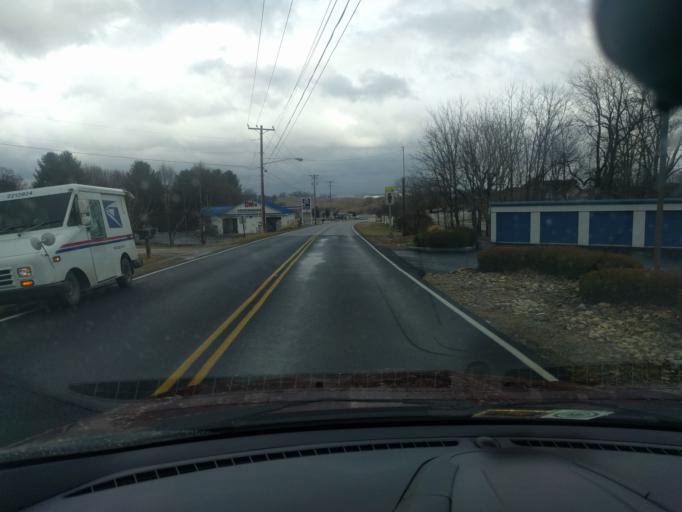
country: US
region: Virginia
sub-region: Pulaski County
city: Pulaski
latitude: 37.0580
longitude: -80.7455
